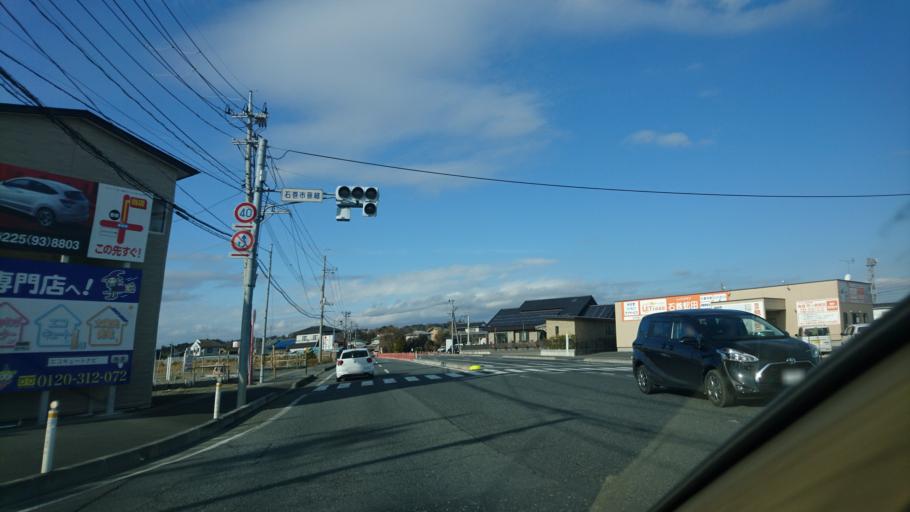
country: JP
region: Miyagi
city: Ishinomaki
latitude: 38.4523
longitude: 141.2648
